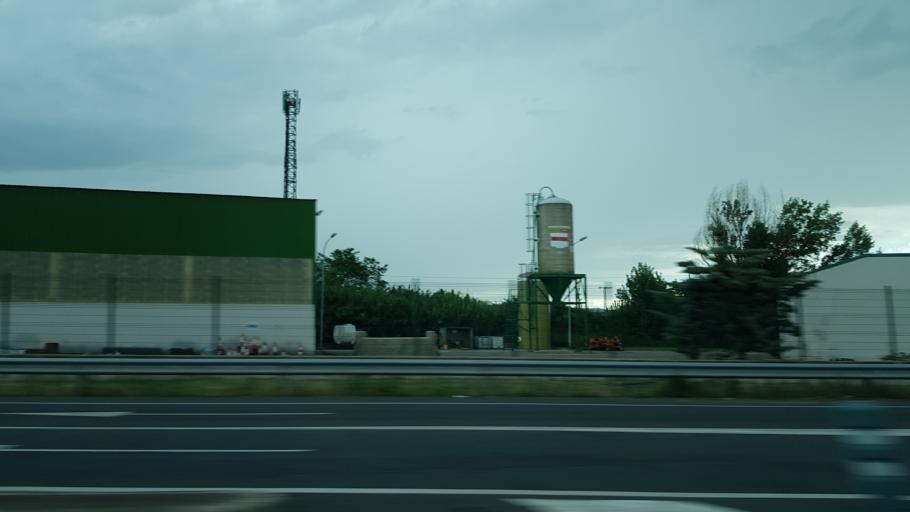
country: ES
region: La Rioja
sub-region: Provincia de La Rioja
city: Lardero
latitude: 42.3952
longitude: -2.4734
